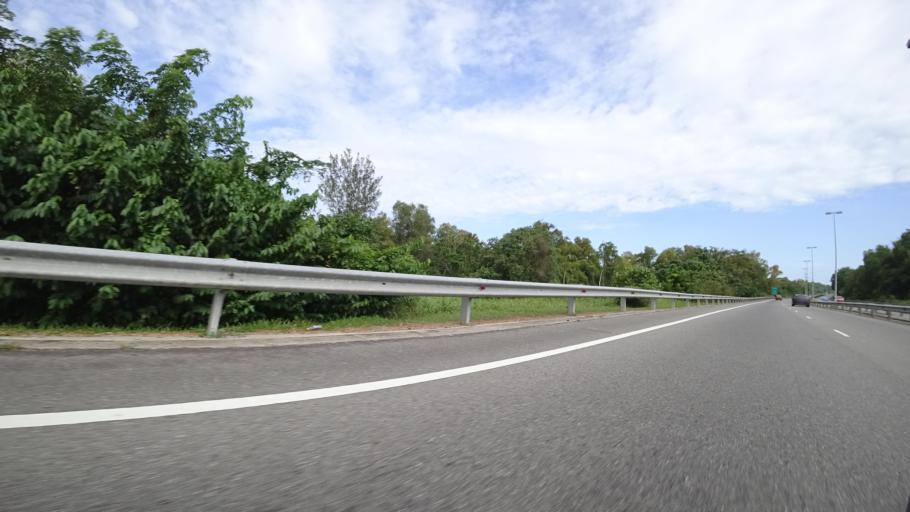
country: BN
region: Brunei and Muara
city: Bandar Seri Begawan
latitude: 4.9320
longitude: 114.9118
